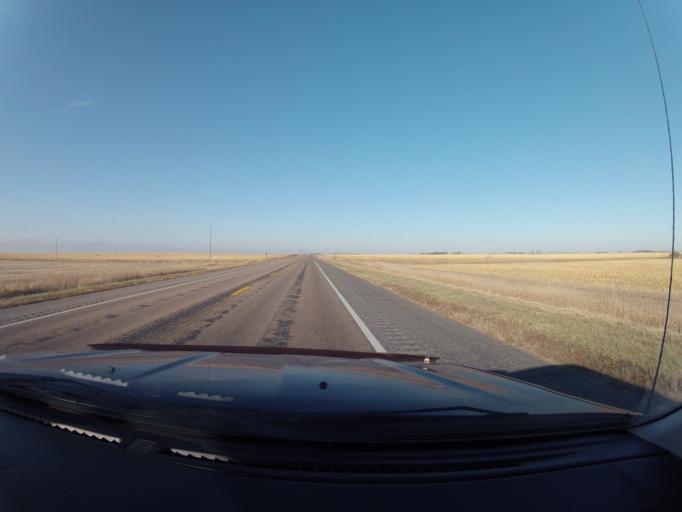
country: US
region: Nebraska
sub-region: Kearney County
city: Minden
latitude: 40.5528
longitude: -98.9518
